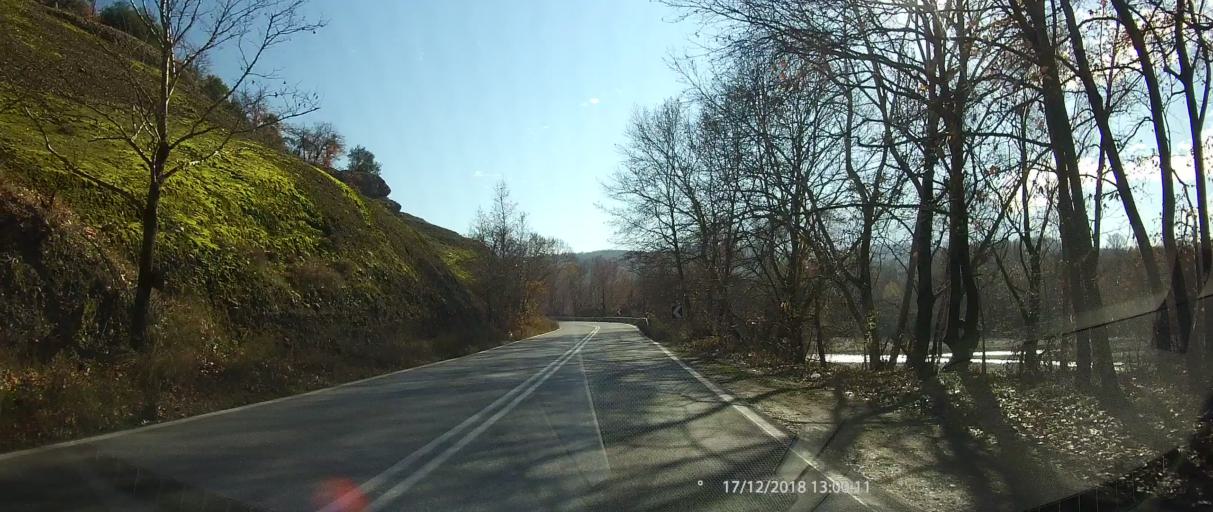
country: GR
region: Thessaly
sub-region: Trikala
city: Kastraki
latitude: 39.7303
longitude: 21.5646
